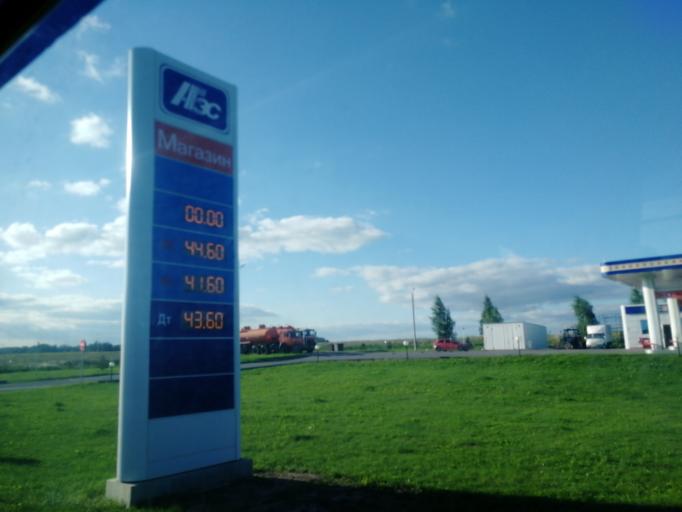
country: RU
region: Tula
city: Dubna
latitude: 54.2825
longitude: 37.1612
